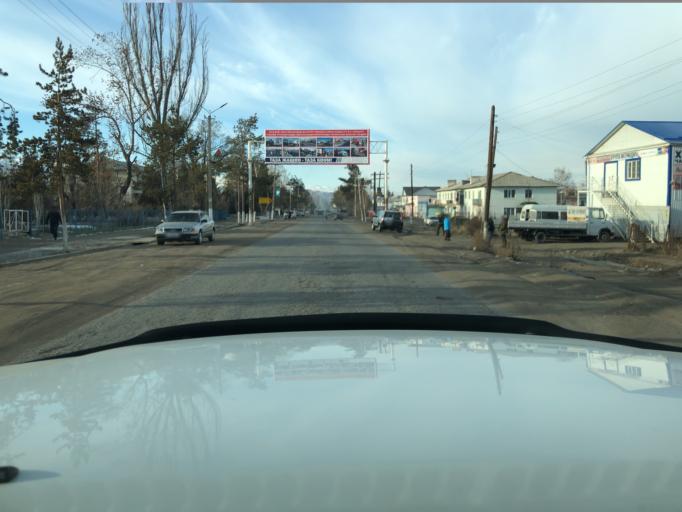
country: KG
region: Ysyk-Koel
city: Pokrovka
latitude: 42.3428
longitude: 78.0064
